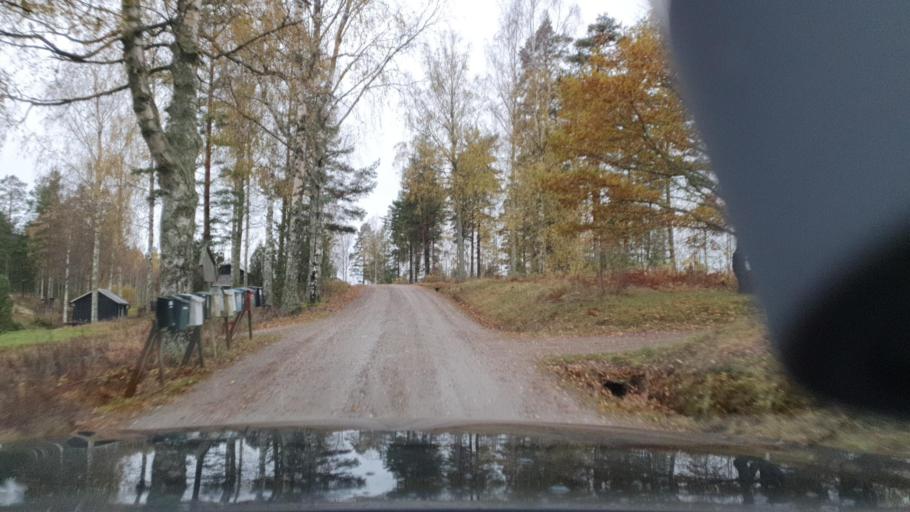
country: SE
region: Vaermland
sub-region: Karlstads Kommun
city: Edsvalla
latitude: 59.5997
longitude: 12.9208
